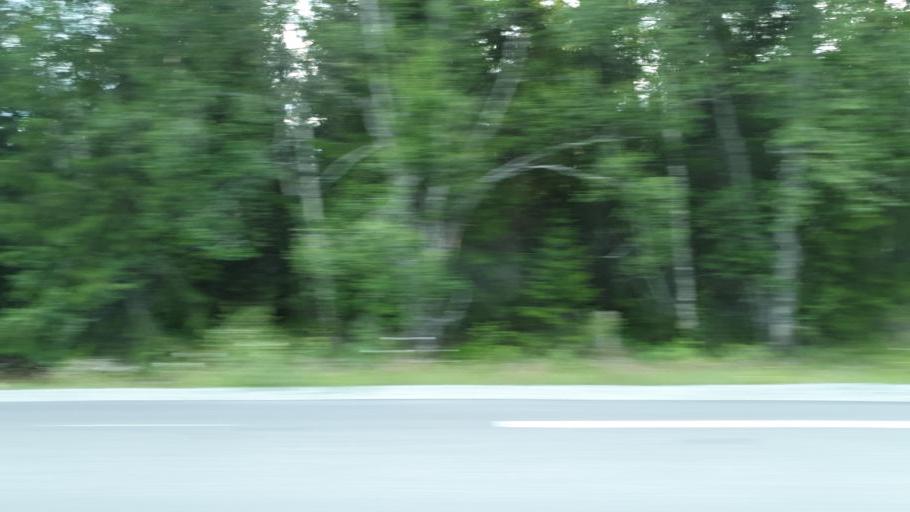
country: NO
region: Oppland
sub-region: Vestre Slidre
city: Slidre
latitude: 61.2350
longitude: 8.9271
